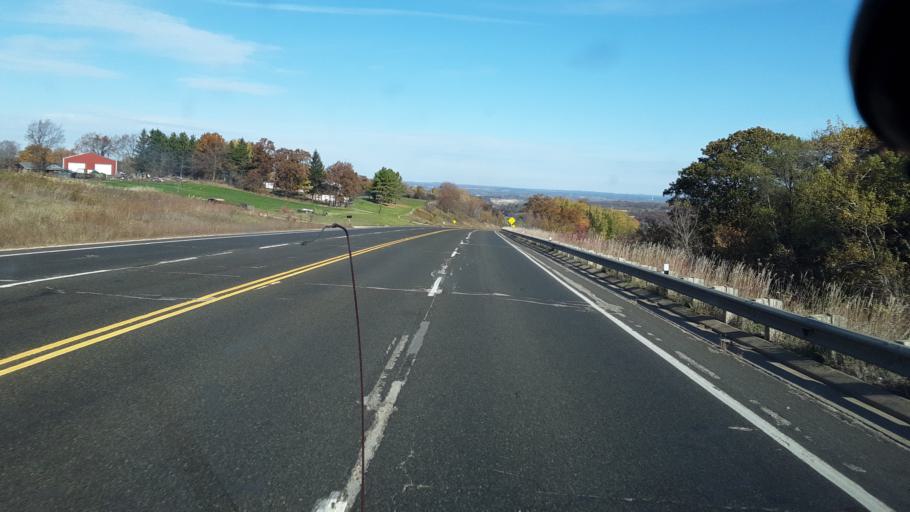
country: US
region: Wisconsin
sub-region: Monroe County
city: Tomah
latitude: 43.9013
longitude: -90.4914
